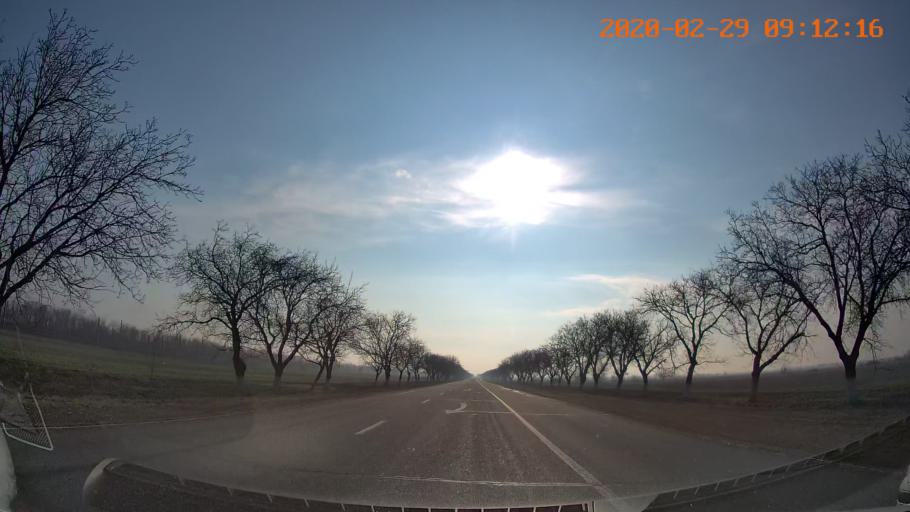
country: MD
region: Telenesti
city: Slobozia
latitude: 46.8281
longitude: 29.8139
